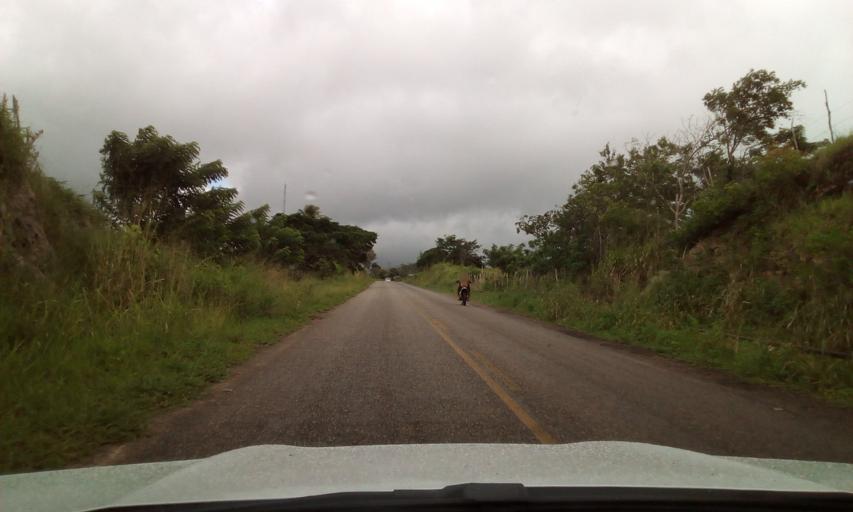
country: BR
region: Paraiba
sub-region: Areia
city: Areia
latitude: -6.8987
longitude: -35.6463
